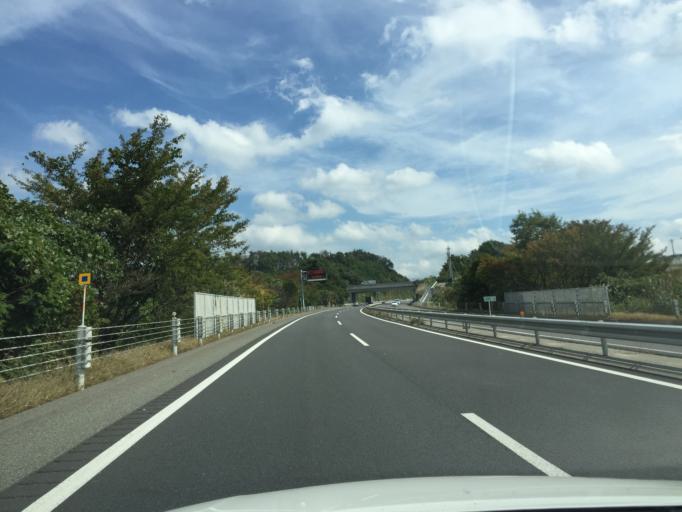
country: JP
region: Fukushima
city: Miharu
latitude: 37.4381
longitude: 140.5150
